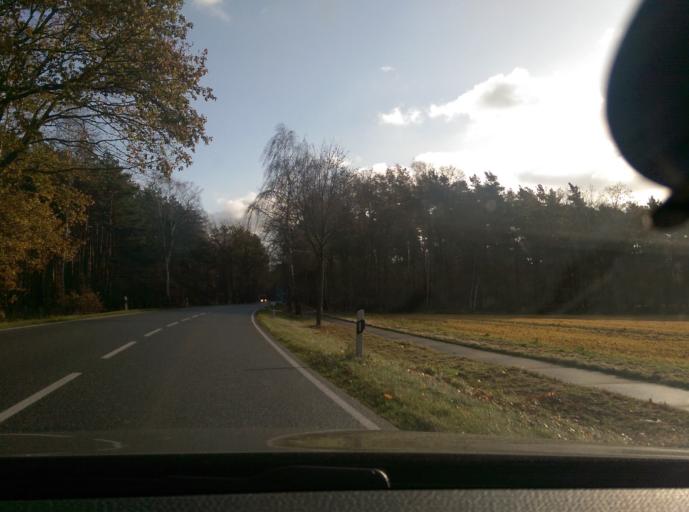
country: DE
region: Lower Saxony
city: Lindwedel
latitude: 52.6678
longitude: 9.7348
